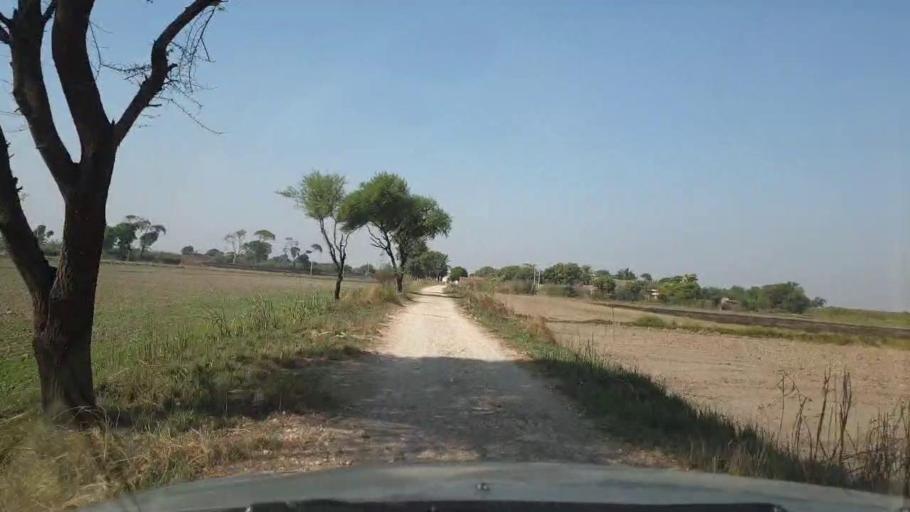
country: PK
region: Sindh
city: Tando Muhammad Khan
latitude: 24.9914
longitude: 68.5010
